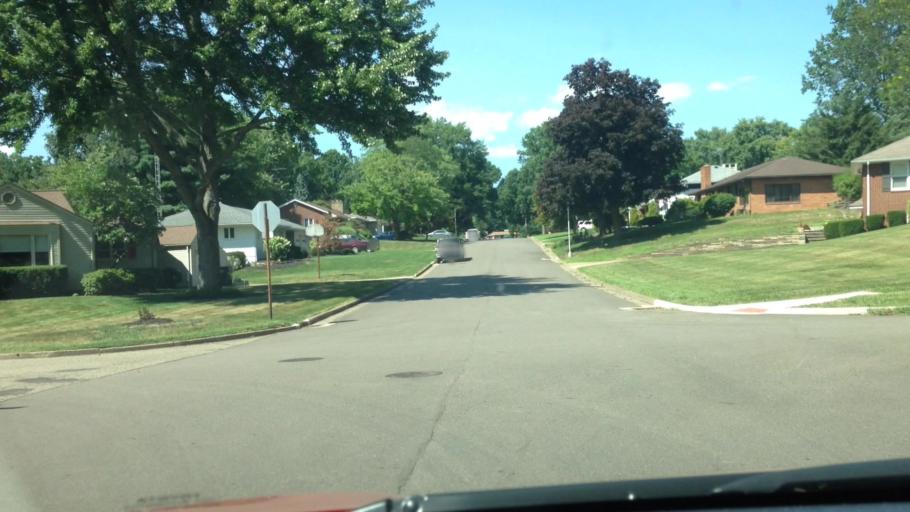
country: US
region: Ohio
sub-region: Stark County
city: Massillon
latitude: 40.8146
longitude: -81.5152
